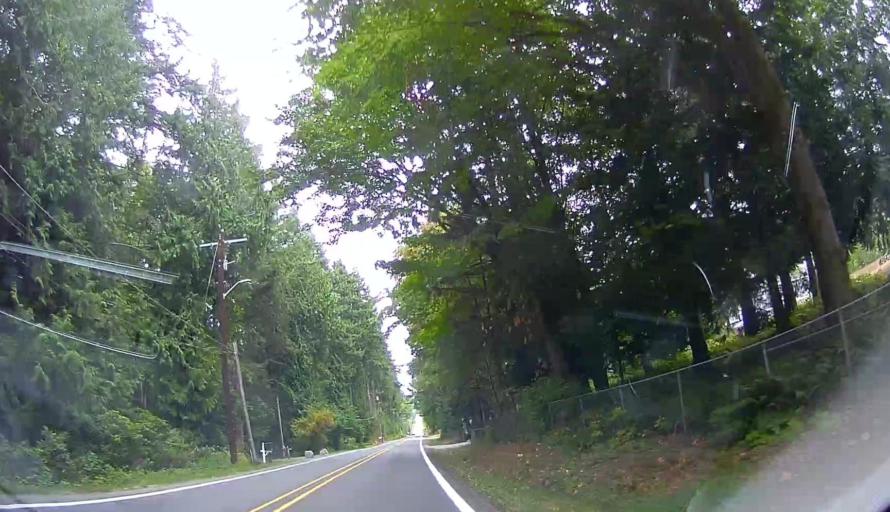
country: US
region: Washington
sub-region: Snohomish County
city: Warm Beach
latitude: 48.1531
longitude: -122.3610
